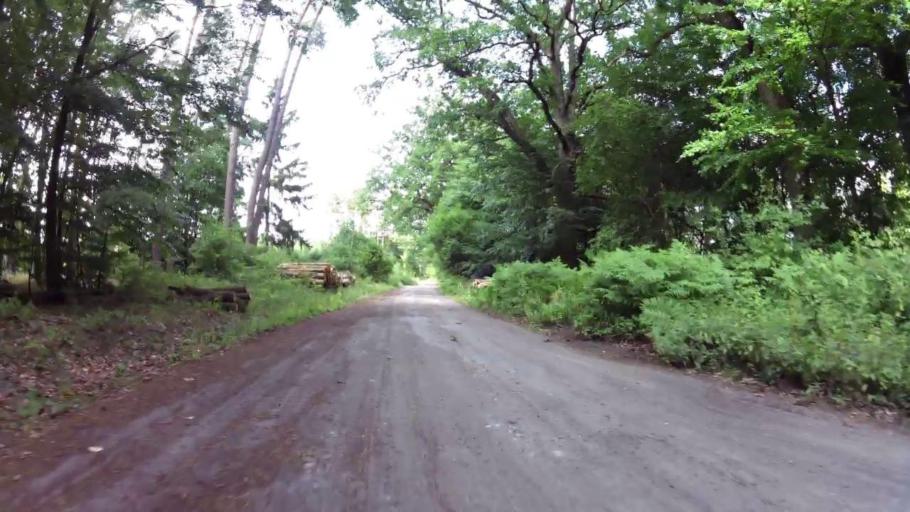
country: PL
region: West Pomeranian Voivodeship
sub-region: Powiat lobeski
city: Lobez
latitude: 53.5957
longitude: 15.6565
